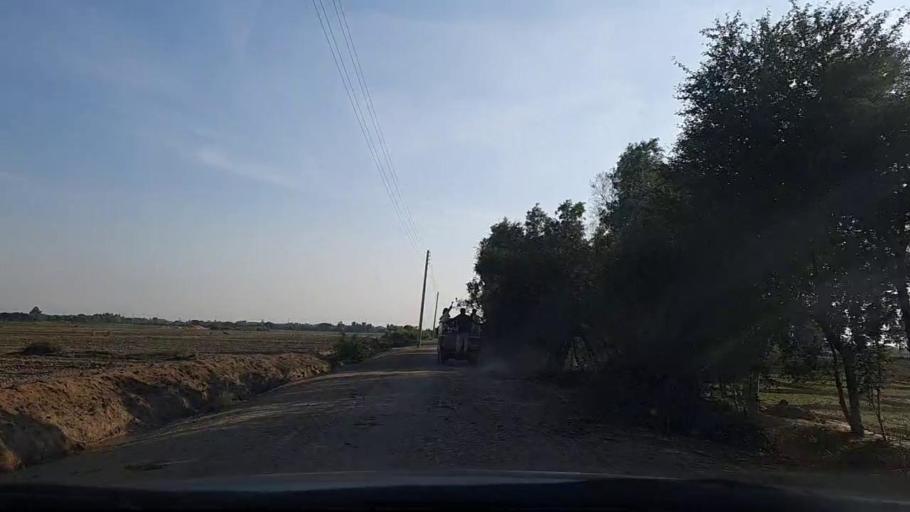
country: PK
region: Sindh
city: Mirpur Sakro
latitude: 24.5314
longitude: 67.6329
